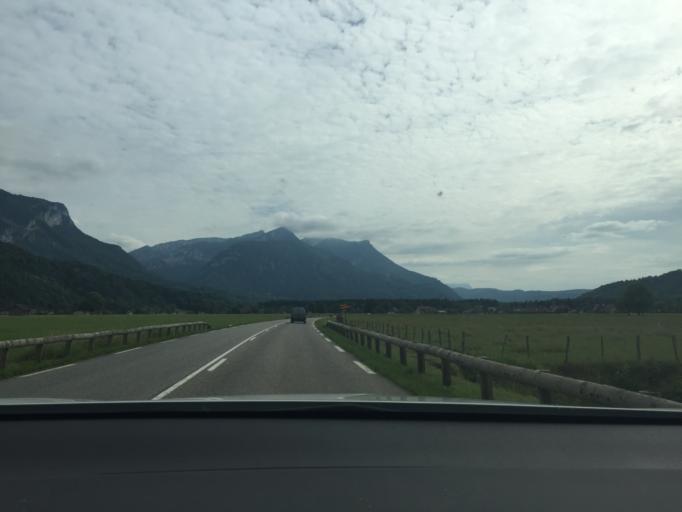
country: FR
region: Rhone-Alpes
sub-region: Departement de la Savoie
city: Les Echelles
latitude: 45.4318
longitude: 5.7647
